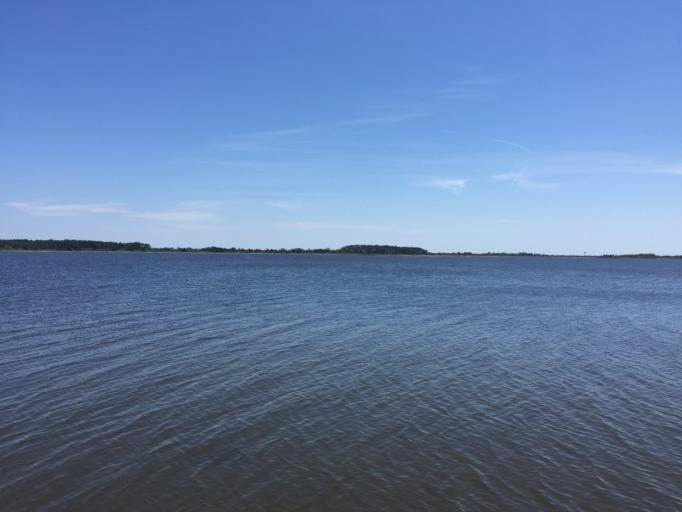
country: US
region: North Carolina
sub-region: Dare County
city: Nags Head
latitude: 35.9002
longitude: -75.6105
